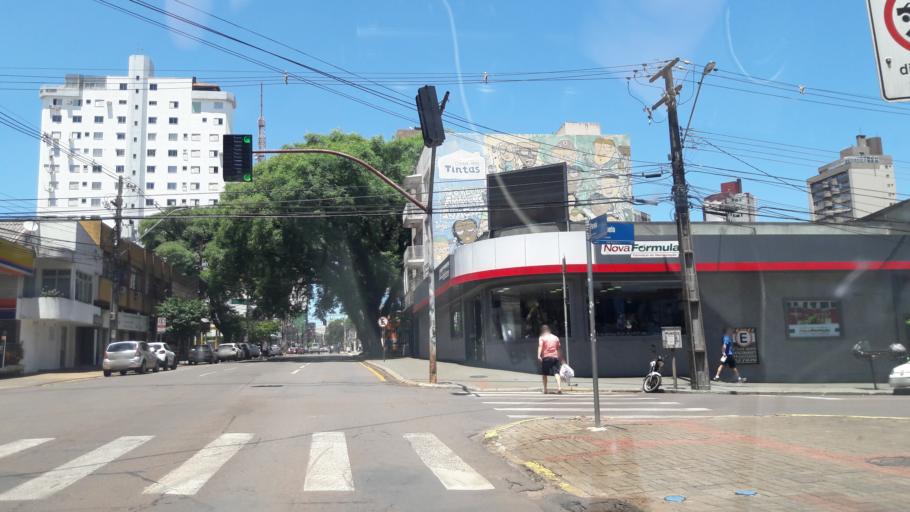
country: BR
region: Parana
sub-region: Cascavel
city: Cascavel
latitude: -24.9517
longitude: -53.4510
